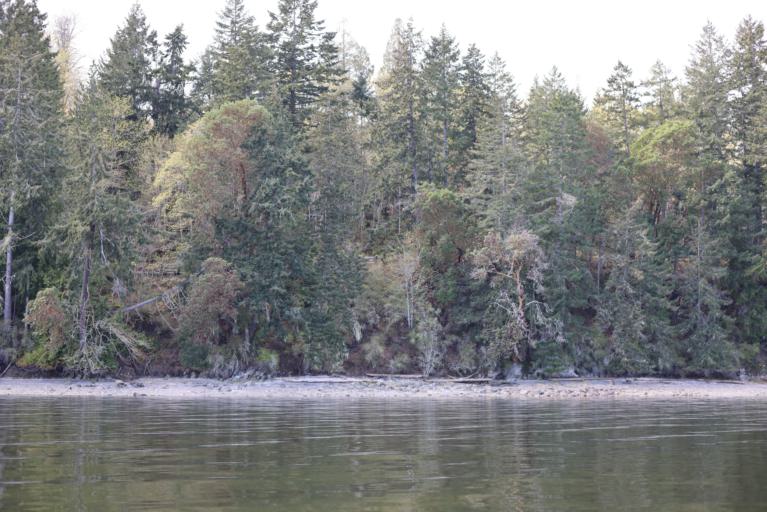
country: CA
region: British Columbia
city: North Saanich
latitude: 48.6254
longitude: -123.5250
